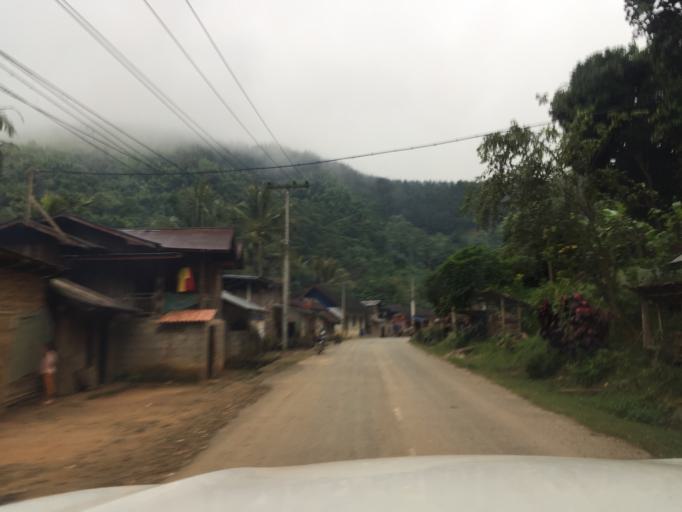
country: LA
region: Phongsali
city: Khoa
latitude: 21.0704
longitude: 102.3761
